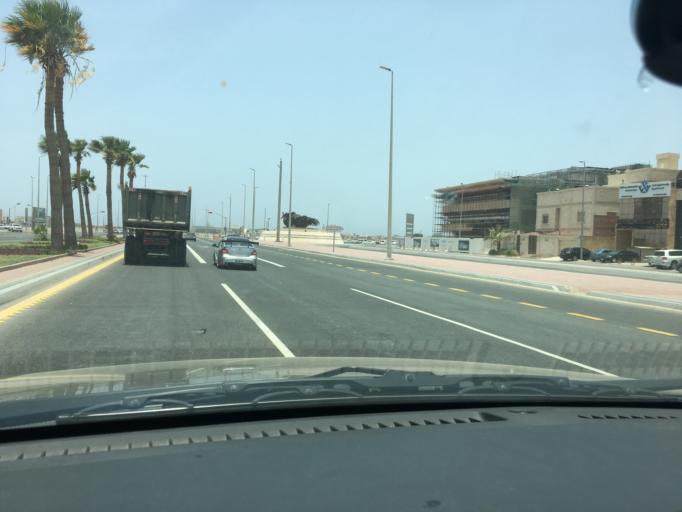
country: SA
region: Makkah
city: Jeddah
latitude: 21.6691
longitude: 39.1232
